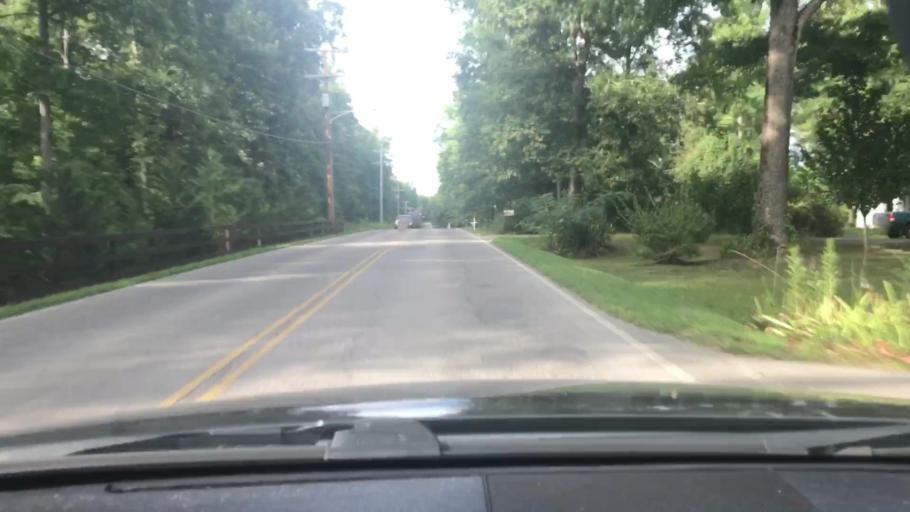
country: US
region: Tennessee
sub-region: Dickson County
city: White Bluff
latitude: 36.0744
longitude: -87.2220
